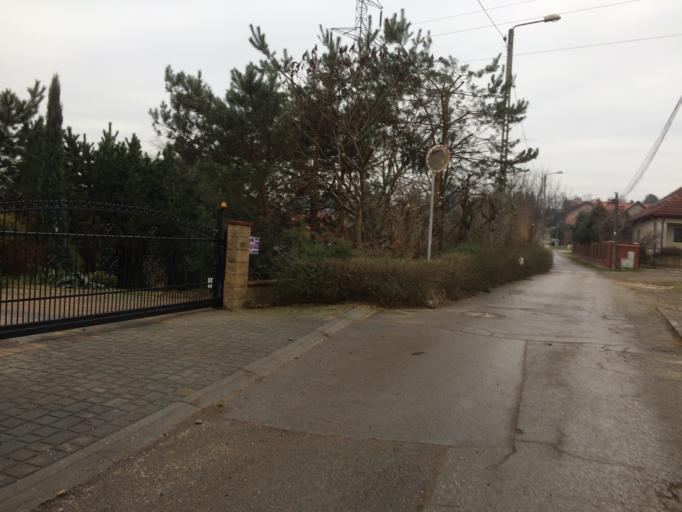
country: PL
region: Lesser Poland Voivodeship
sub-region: Powiat wielicki
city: Czarnochowice
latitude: 50.0025
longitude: 20.0400
